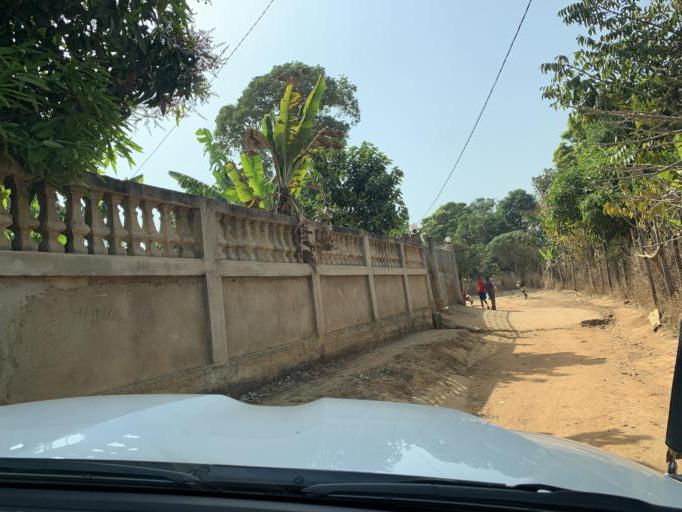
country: GN
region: Mamou
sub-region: Dalaba
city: Dalaba
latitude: 10.7657
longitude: -12.2821
